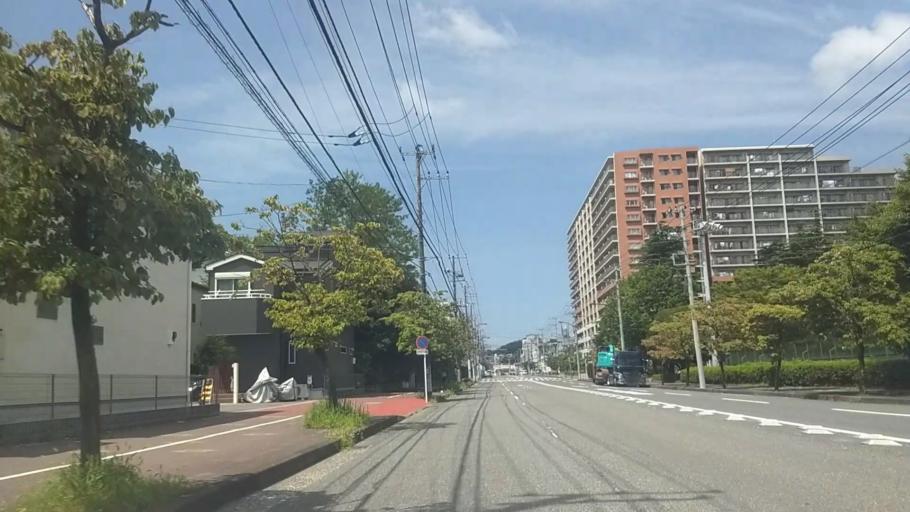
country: JP
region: Kanagawa
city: Yokosuka
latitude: 35.3169
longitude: 139.6355
